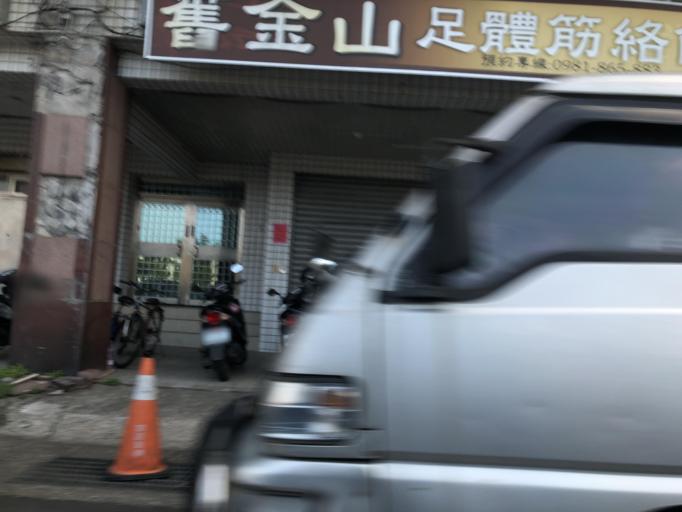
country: TW
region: Taiwan
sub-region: Keelung
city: Keelung
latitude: 25.2198
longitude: 121.6362
